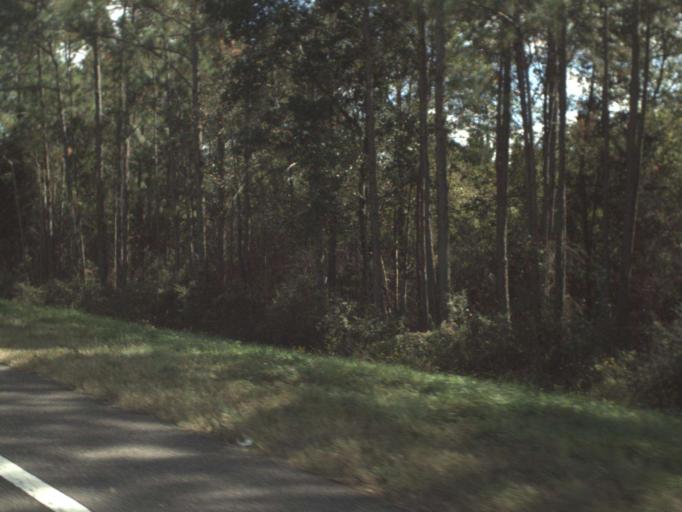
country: US
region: Florida
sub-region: Okaloosa County
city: Crestview
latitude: 30.7575
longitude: -86.5376
